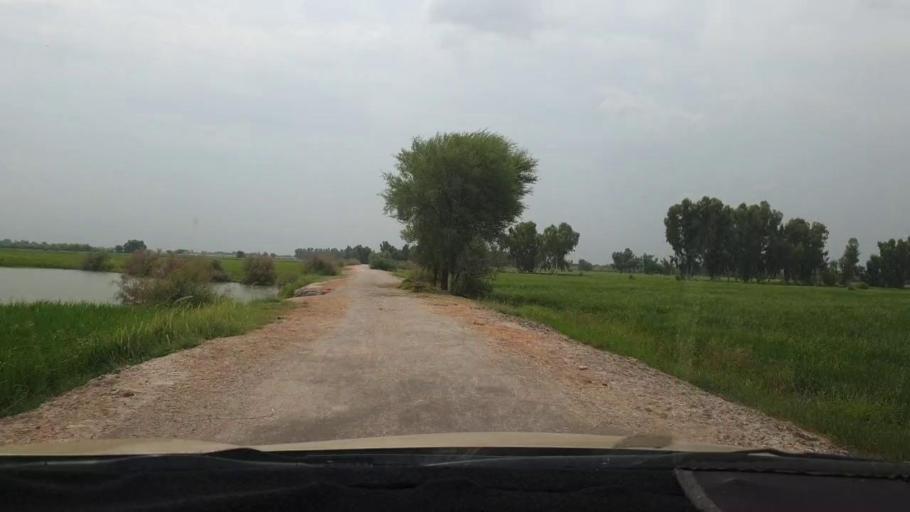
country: PK
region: Sindh
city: Naudero
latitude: 27.6265
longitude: 68.3211
